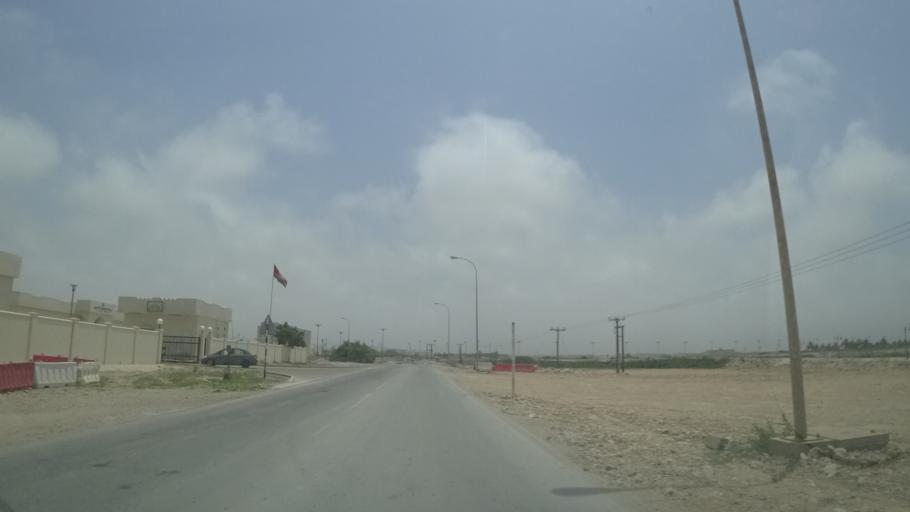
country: OM
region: Zufar
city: Salalah
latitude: 17.0226
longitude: 54.1738
